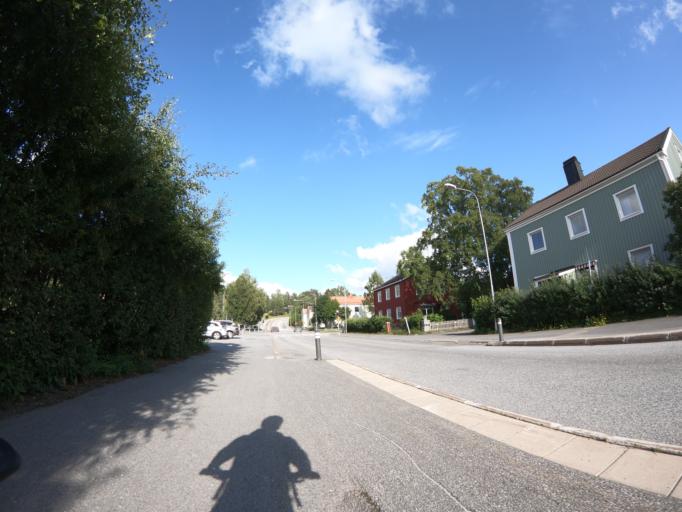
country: SE
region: Vaesterbotten
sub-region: Umea Kommun
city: Umea
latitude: 63.8278
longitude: 20.2844
